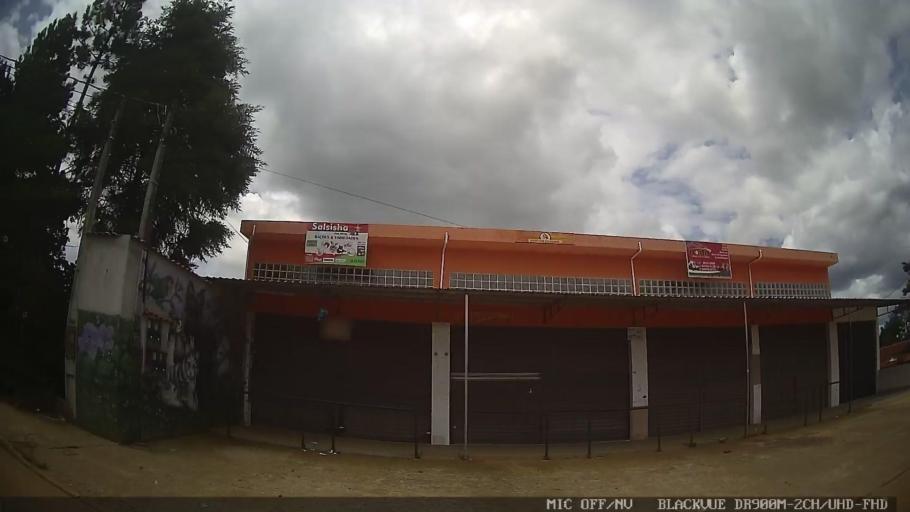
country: BR
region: Sao Paulo
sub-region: Suzano
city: Suzano
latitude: -23.6032
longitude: -46.2464
